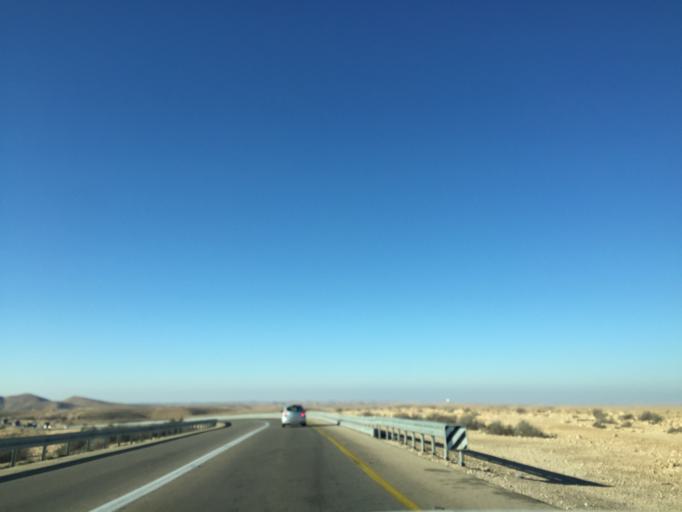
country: IL
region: Southern District
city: Mitzpe Ramon
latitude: 30.6798
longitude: 34.8014
